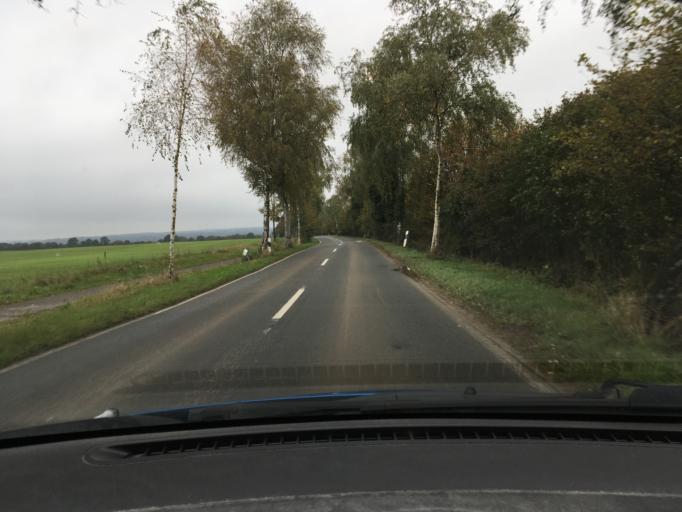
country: DE
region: Schleswig-Holstein
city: Bosau
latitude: 54.1001
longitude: 10.4501
